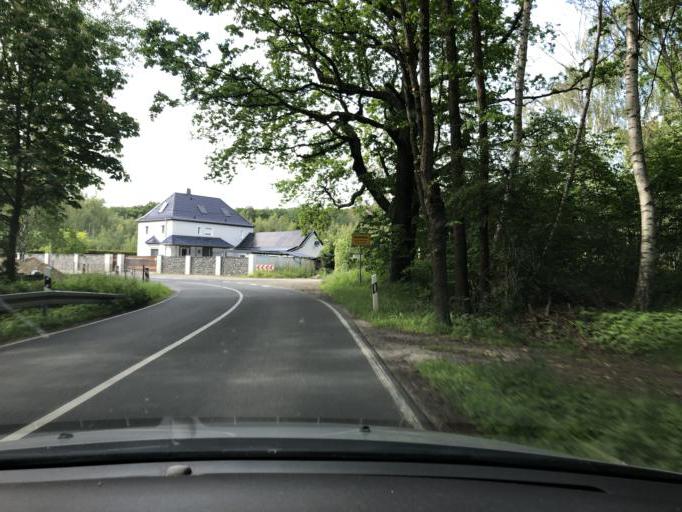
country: DE
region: Saxony
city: Brandis
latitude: 51.2929
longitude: 12.6517
